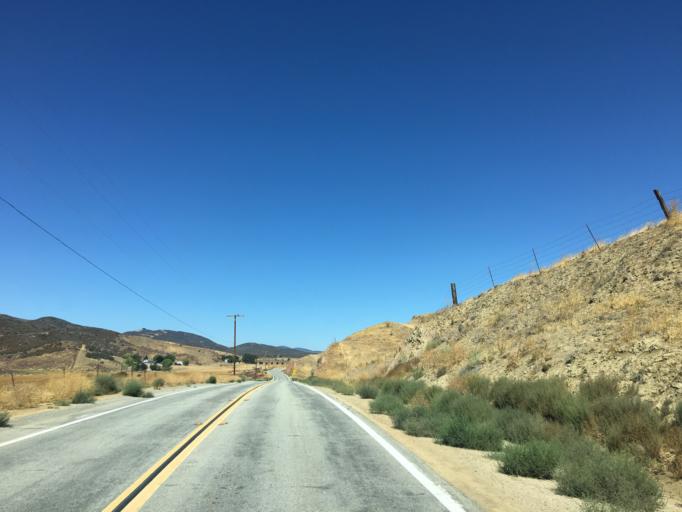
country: US
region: California
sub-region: Los Angeles County
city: Leona Valley
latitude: 34.6382
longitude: -118.3471
